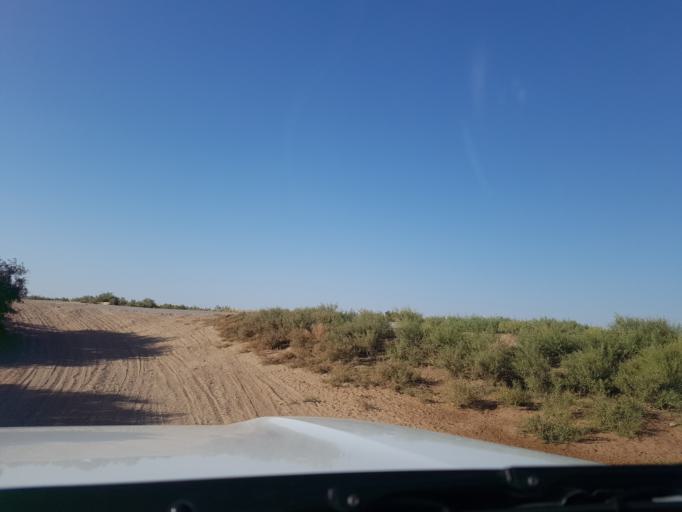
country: IR
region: Razavi Khorasan
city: Sarakhs
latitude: 36.9958
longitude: 61.3879
